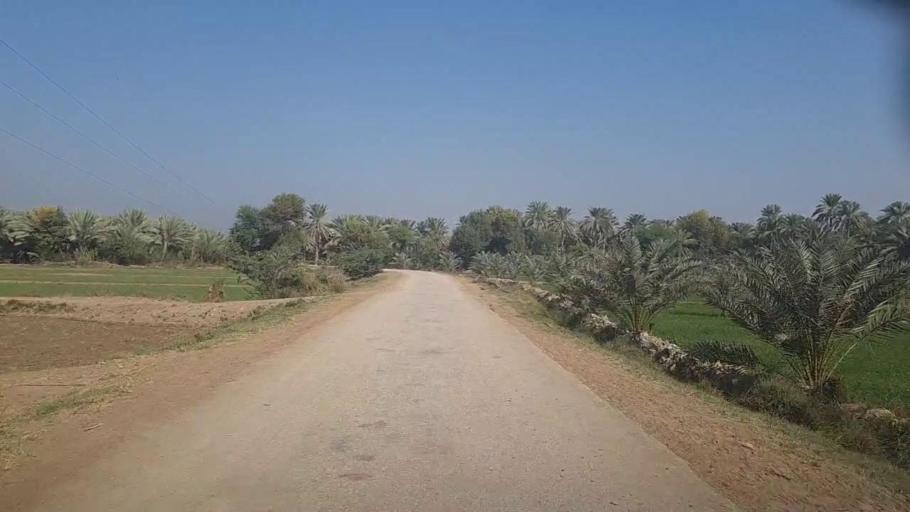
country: PK
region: Sindh
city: Kot Diji
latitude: 27.4209
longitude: 68.7061
